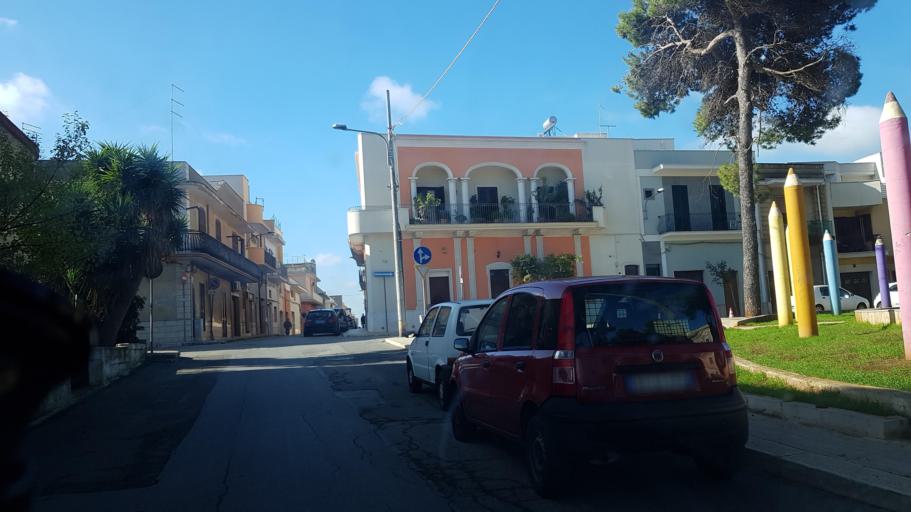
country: IT
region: Apulia
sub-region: Provincia di Brindisi
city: San Vito dei Normanni
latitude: 40.6556
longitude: 17.7004
